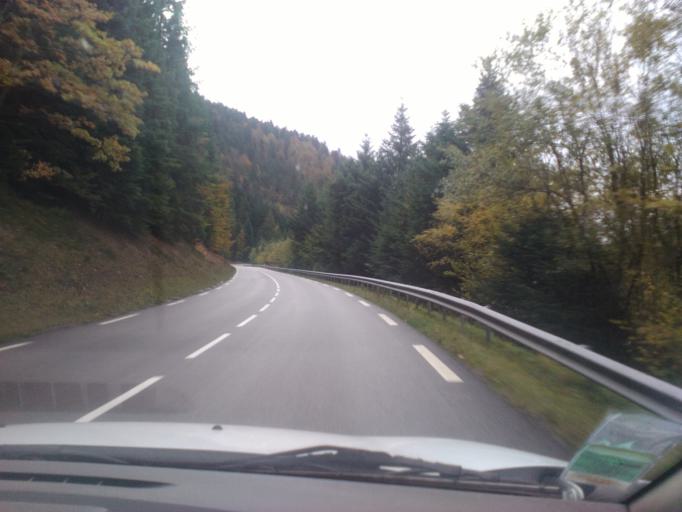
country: FR
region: Lorraine
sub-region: Departement des Vosges
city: Xonrupt-Longemer
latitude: 48.1154
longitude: 6.9104
